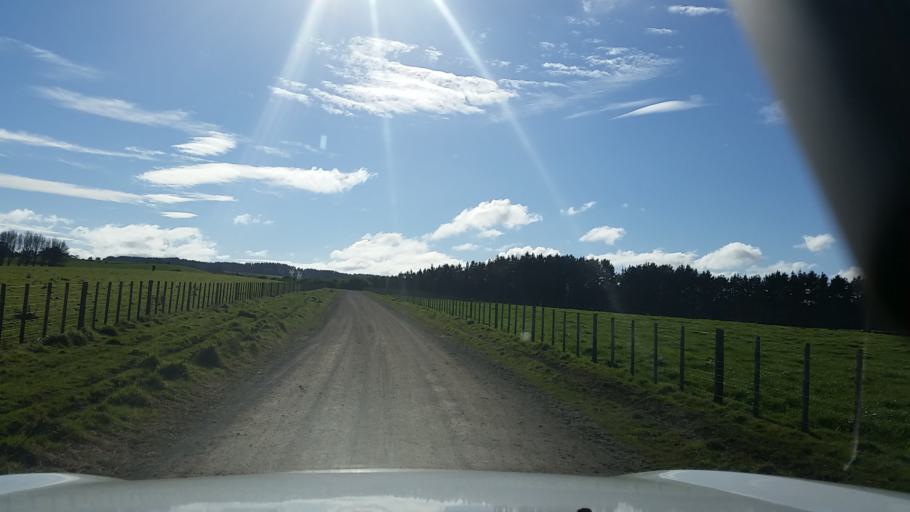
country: NZ
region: Taranaki
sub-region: South Taranaki District
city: Patea
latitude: -39.7076
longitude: 174.6362
